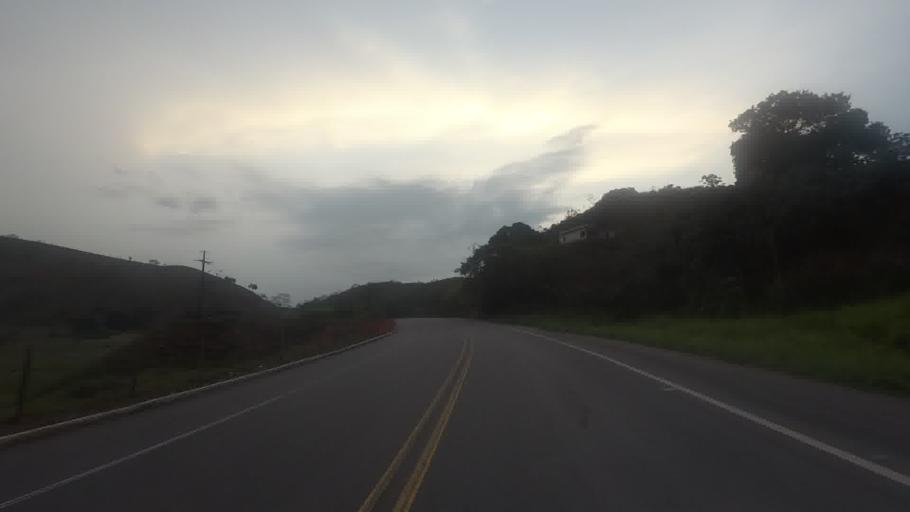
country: BR
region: Minas Gerais
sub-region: Alem Paraiba
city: Alem Paraiba
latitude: -21.8410
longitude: -42.6248
